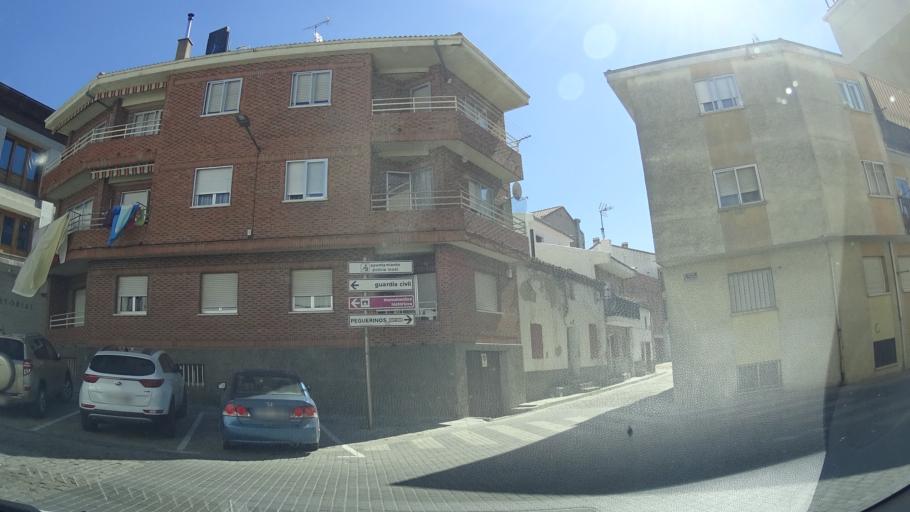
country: ES
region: Castille and Leon
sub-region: Provincia de Avila
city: Las Navas del Marques
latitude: 40.6035
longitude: -4.3276
